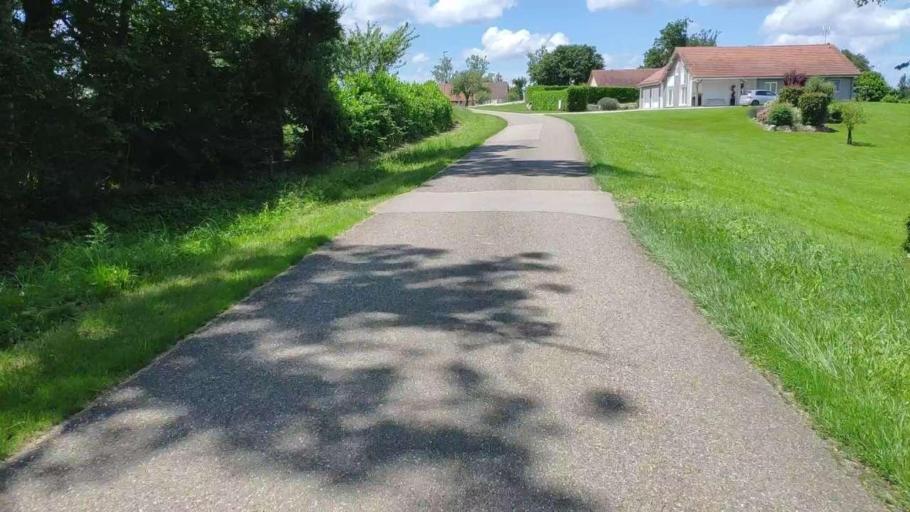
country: FR
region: Franche-Comte
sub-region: Departement du Jura
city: Bletterans
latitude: 46.8469
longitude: 5.4709
